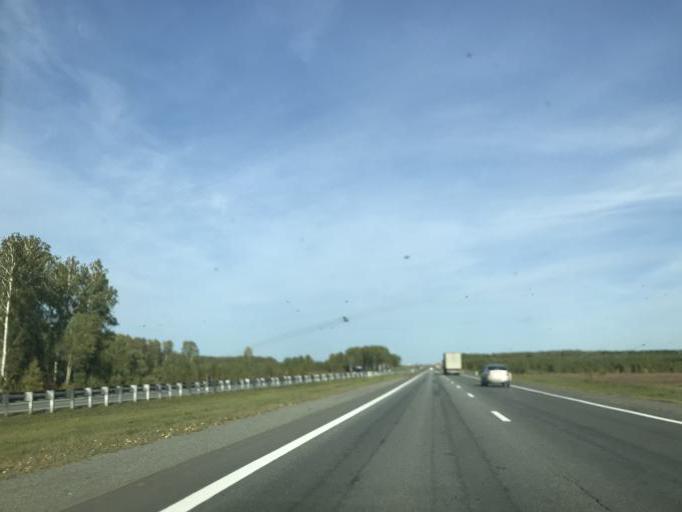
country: RU
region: Chelyabinsk
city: Poletayevo
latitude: 54.9777
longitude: 60.9963
